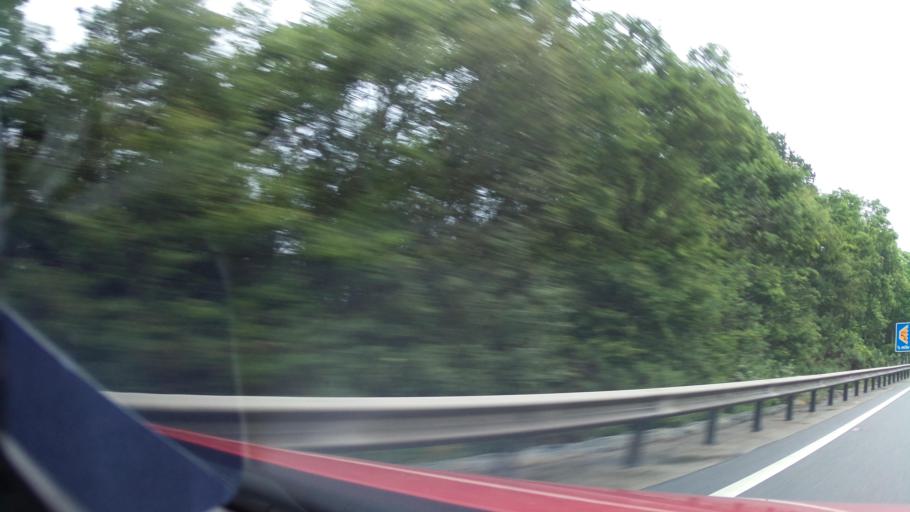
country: GB
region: England
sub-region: Surrey
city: Windlesham
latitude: 51.3666
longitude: -0.6358
